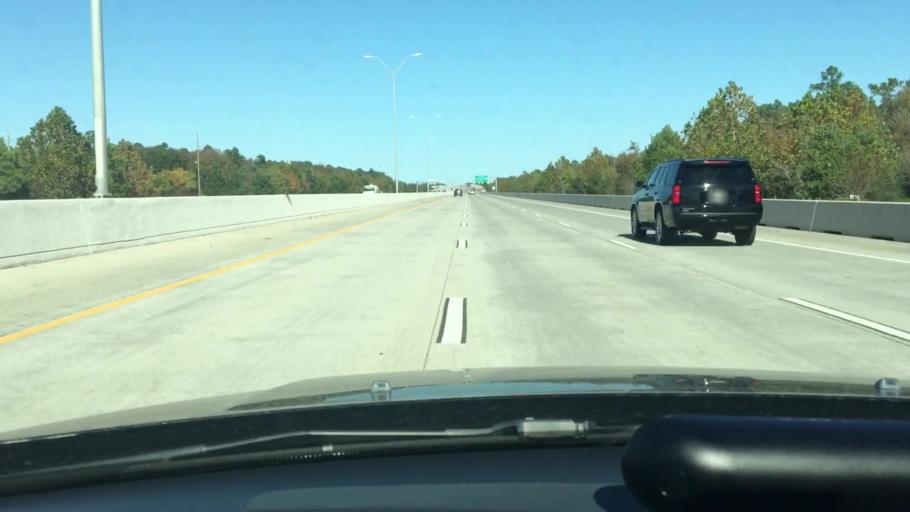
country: US
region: Texas
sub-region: Harris County
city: Sheldon
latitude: 29.8613
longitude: -95.1870
